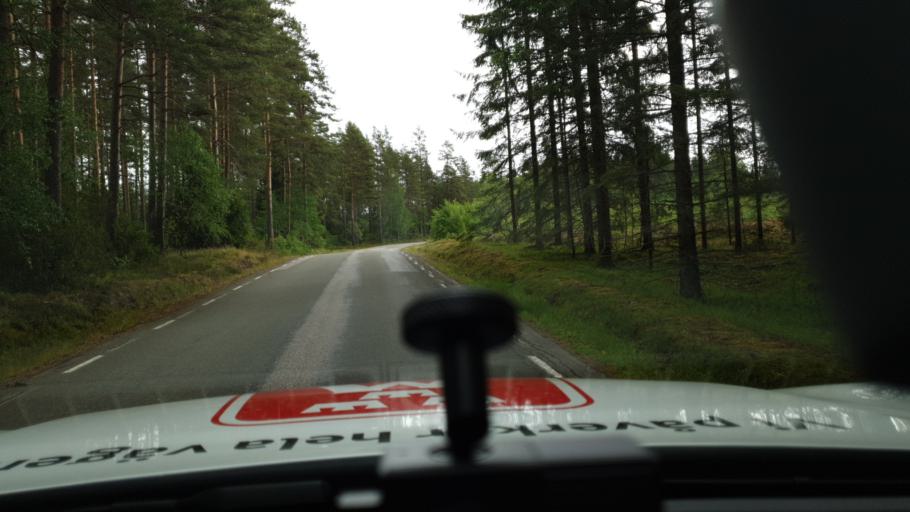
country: SE
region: Vaestra Goetaland
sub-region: Tibro Kommun
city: Tibro
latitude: 58.4112
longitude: 14.2440
